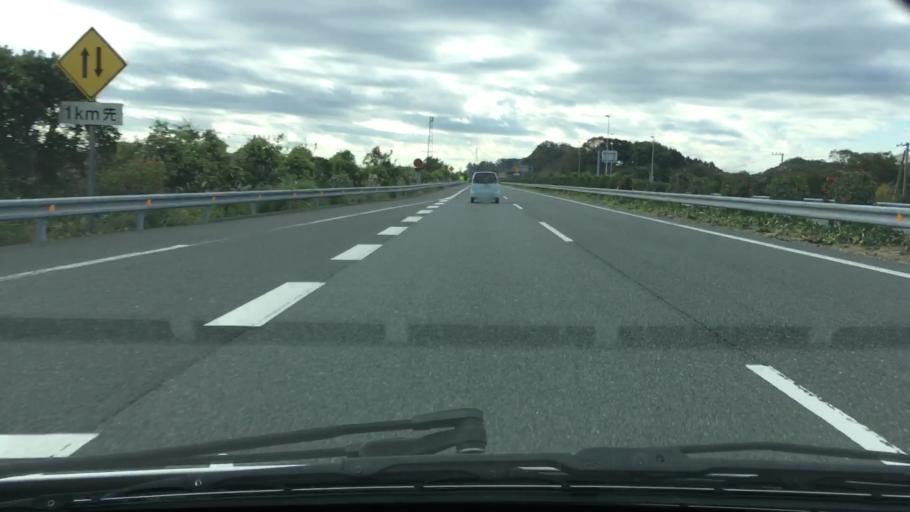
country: JP
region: Chiba
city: Kimitsu
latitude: 35.2507
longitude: 139.8918
